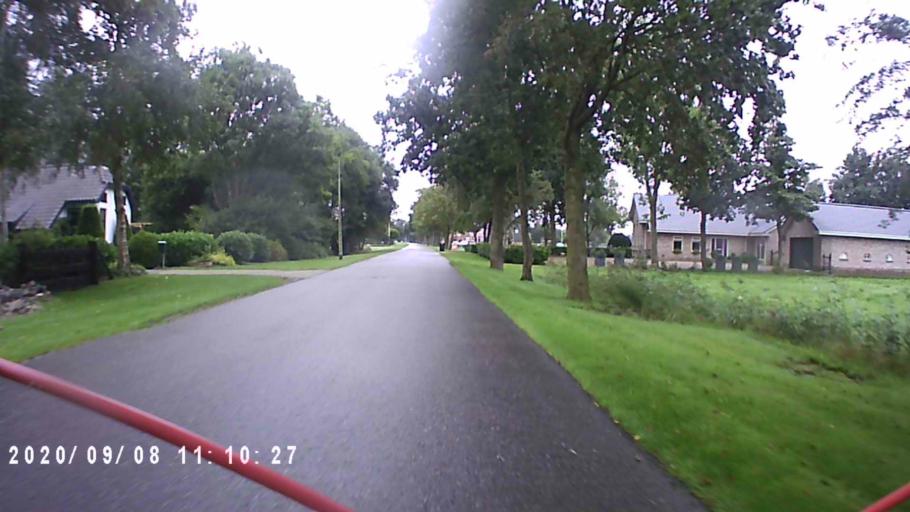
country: NL
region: Groningen
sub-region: Gemeente Hoogezand-Sappemeer
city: Hoogezand
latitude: 53.1834
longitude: 6.7045
